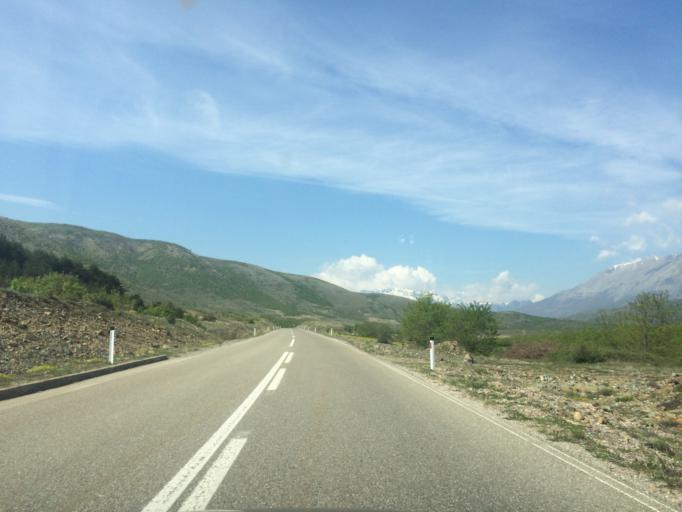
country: XK
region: Gjakova
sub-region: Komuna e Junikut
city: Junik
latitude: 42.4052
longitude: 20.2502
